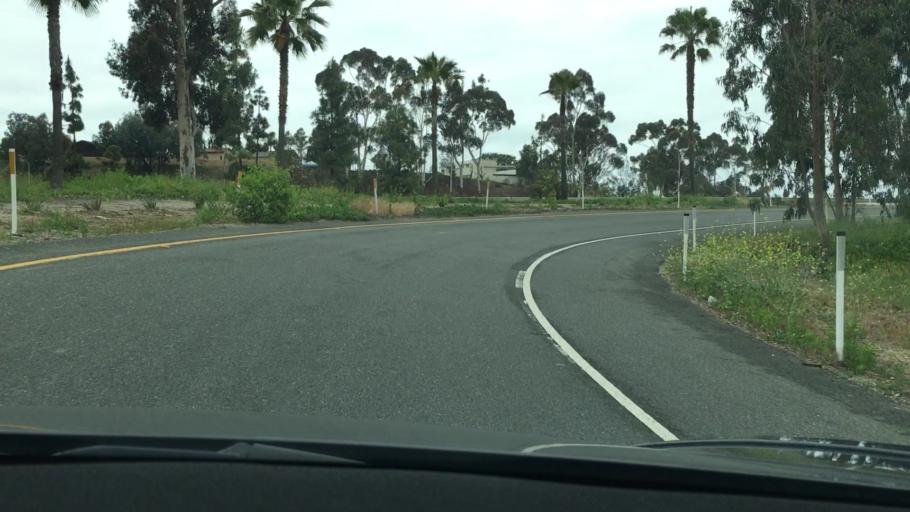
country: US
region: California
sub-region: Orange County
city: Dana Point
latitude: 33.4673
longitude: -117.6679
